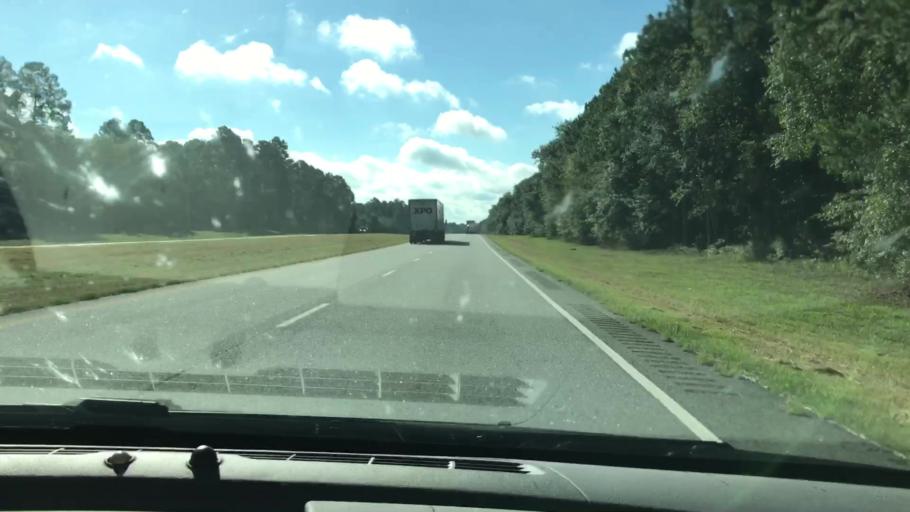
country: US
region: Georgia
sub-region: Dougherty County
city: Putney
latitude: 31.5634
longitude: -84.0142
